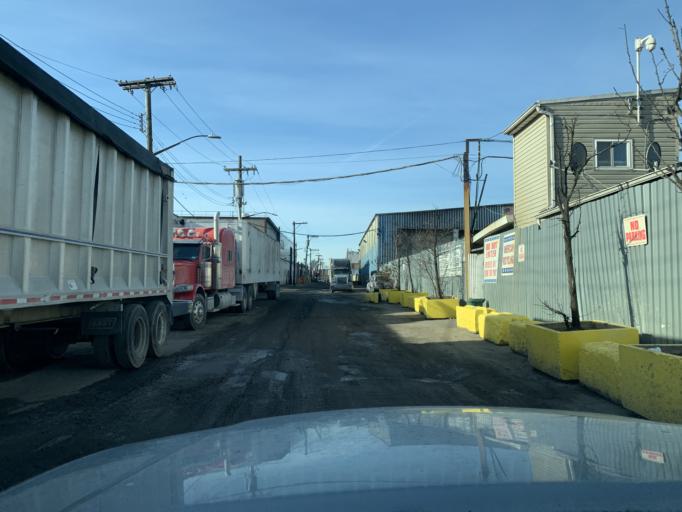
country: US
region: New York
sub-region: Queens County
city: Jamaica
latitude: 40.7051
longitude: -73.7847
